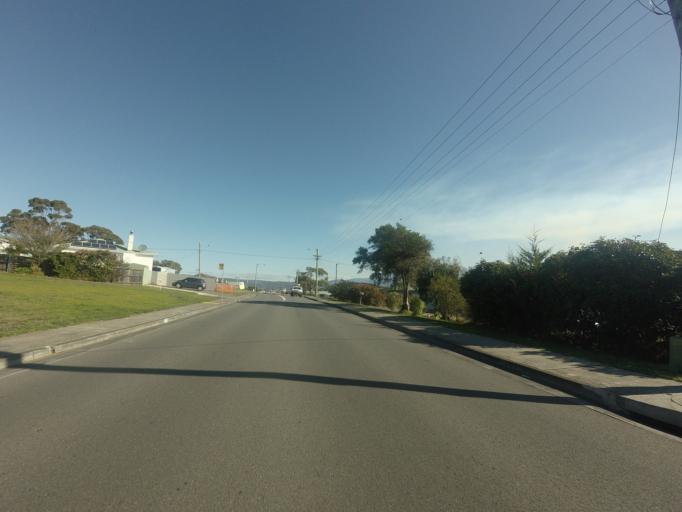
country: AU
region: Tasmania
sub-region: Clarence
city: Warrane
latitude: -42.8593
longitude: 147.3771
